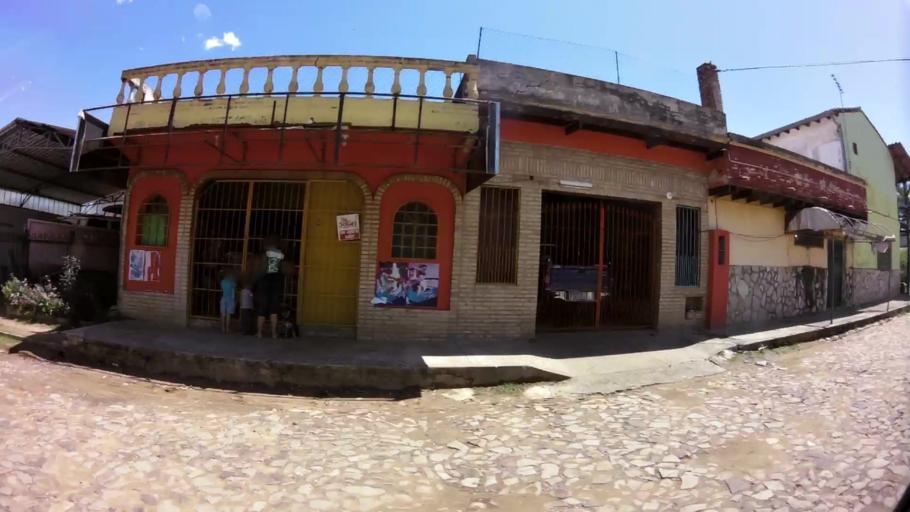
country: PY
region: Central
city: Colonia Mariano Roque Alonso
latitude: -25.1933
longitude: -57.5482
